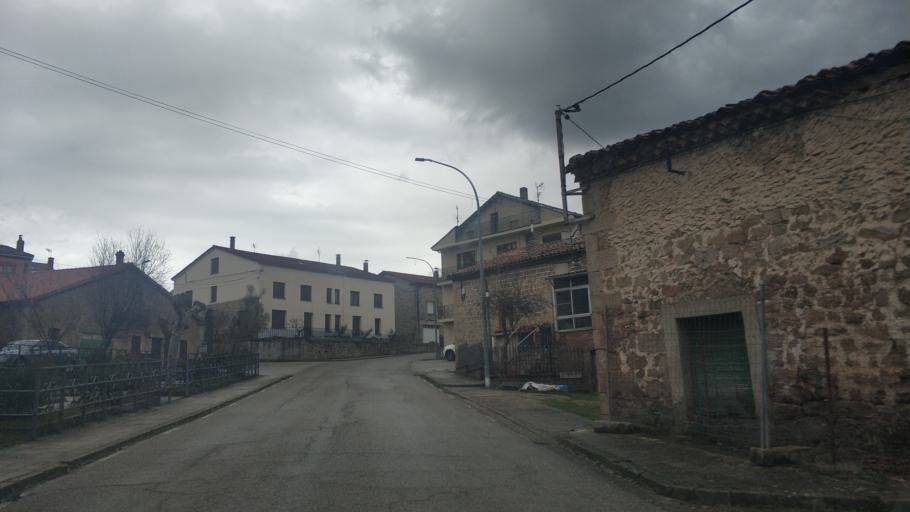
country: ES
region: Castille and Leon
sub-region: Provincia de Burgos
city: Canicosa de la Sierra
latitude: 41.9359
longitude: -3.0396
